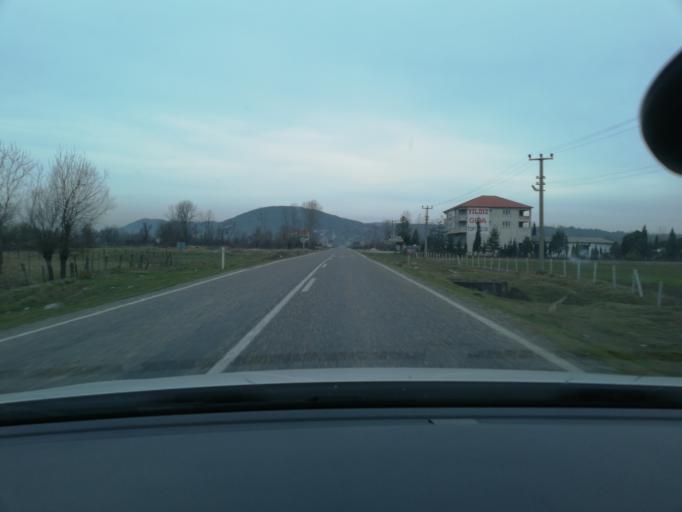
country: TR
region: Zonguldak
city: Saltukova
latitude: 41.5148
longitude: 32.1031
